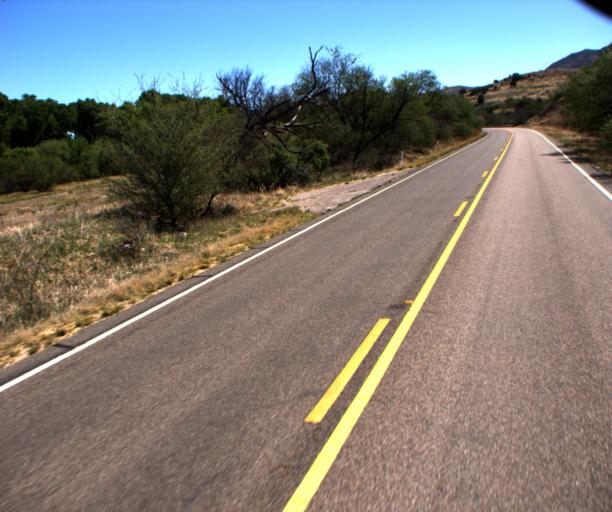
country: US
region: Arizona
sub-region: Santa Cruz County
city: Rio Rico
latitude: 31.5154
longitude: -110.7883
